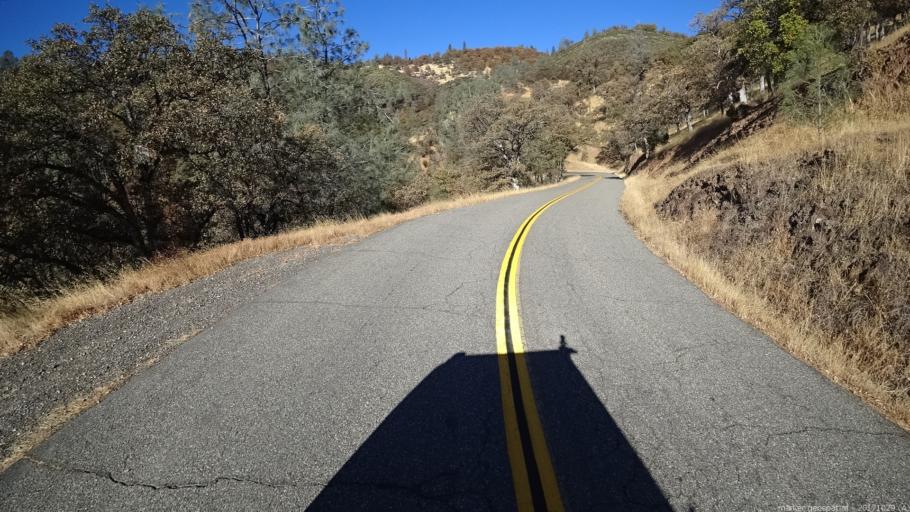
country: US
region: California
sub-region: Trinity County
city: Lewiston
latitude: 40.3774
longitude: -122.8483
